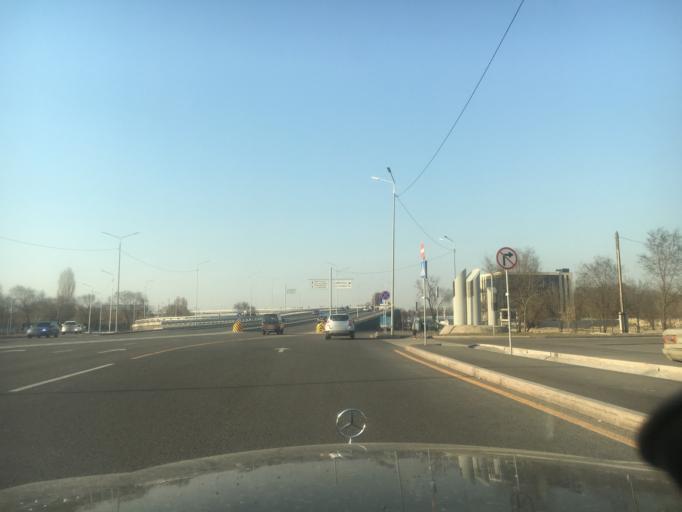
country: KZ
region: Almaty Qalasy
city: Almaty
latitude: 43.2723
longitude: 76.9448
